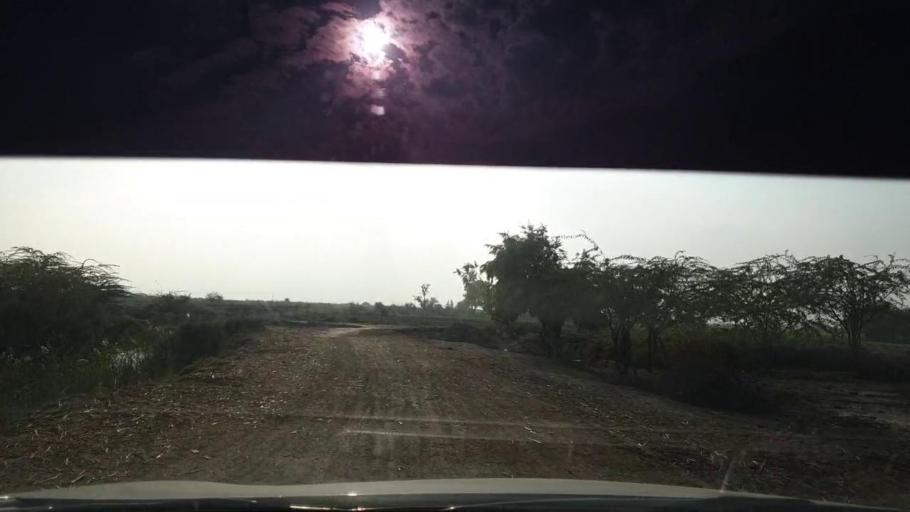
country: PK
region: Sindh
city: Berani
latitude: 25.7497
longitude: 68.9493
